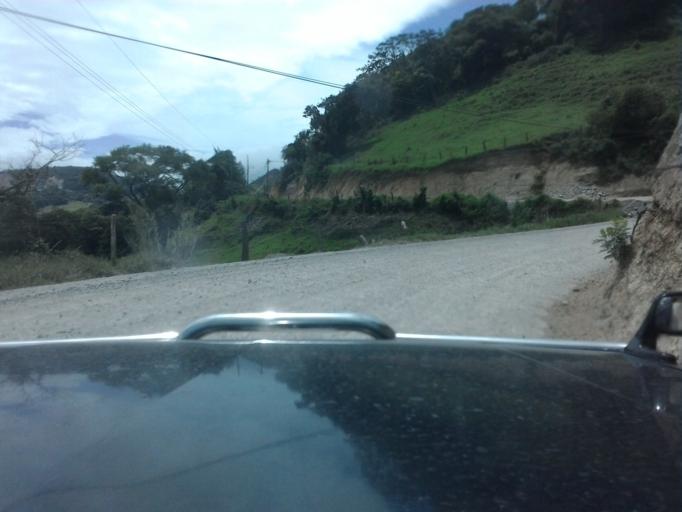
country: CR
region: Guanacaste
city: Juntas
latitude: 10.2840
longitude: -84.8362
